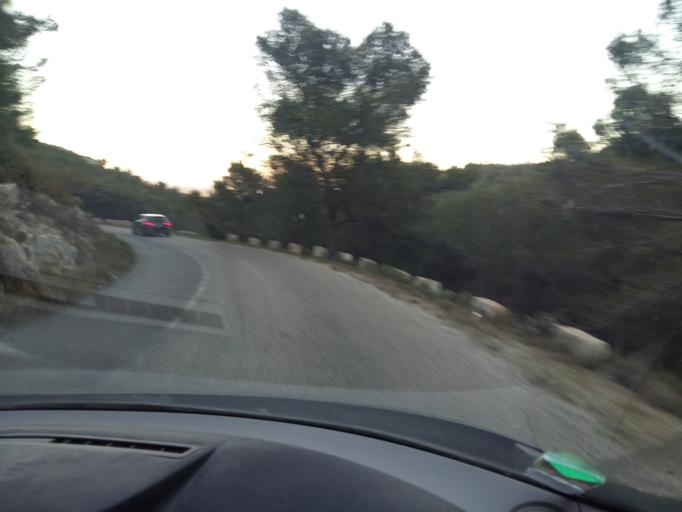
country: FR
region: Provence-Alpes-Cote d'Azur
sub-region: Departement des Bouches-du-Rhone
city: Maussane-les-Alpilles
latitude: 43.7552
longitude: 4.7932
